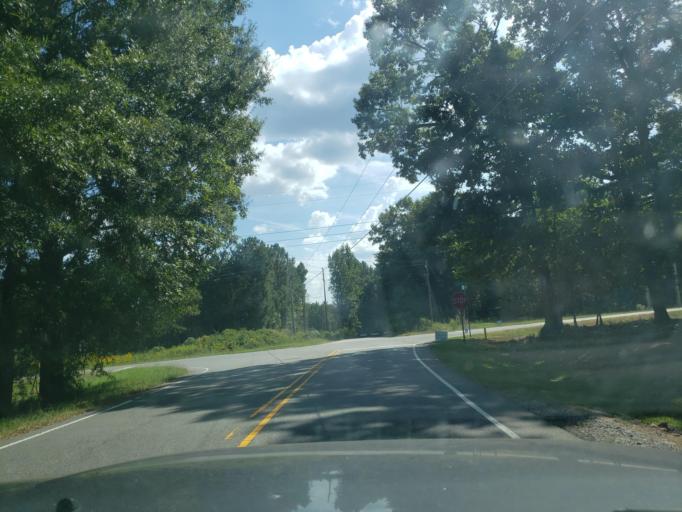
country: US
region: North Carolina
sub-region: Wake County
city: West Raleigh
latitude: 35.9169
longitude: -78.6844
